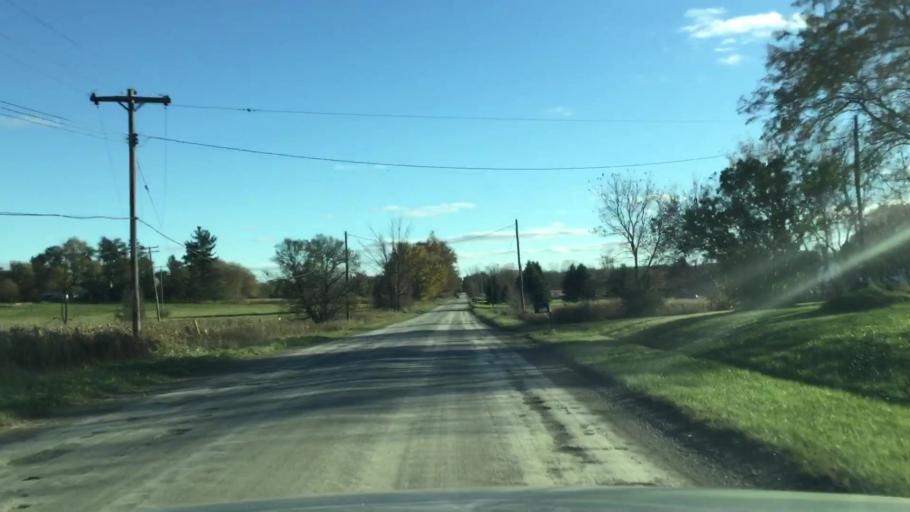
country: US
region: Michigan
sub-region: Lapeer County
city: Lapeer
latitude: 43.0666
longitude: -83.2271
